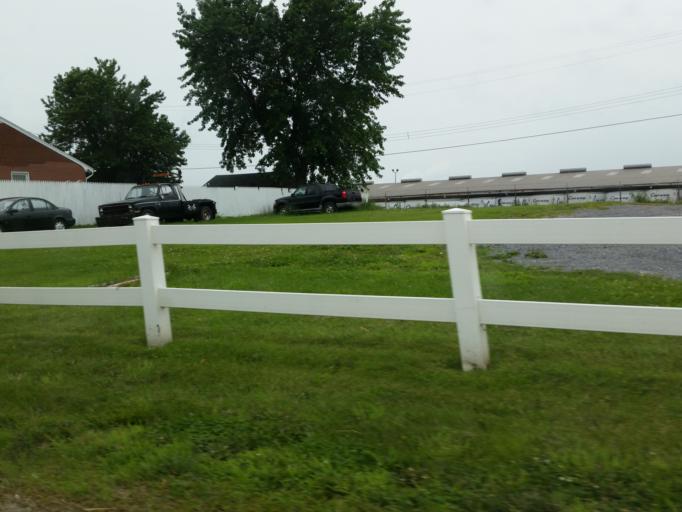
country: US
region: Pennsylvania
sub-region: York County
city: Emigsville
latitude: 40.0207
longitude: -76.7474
